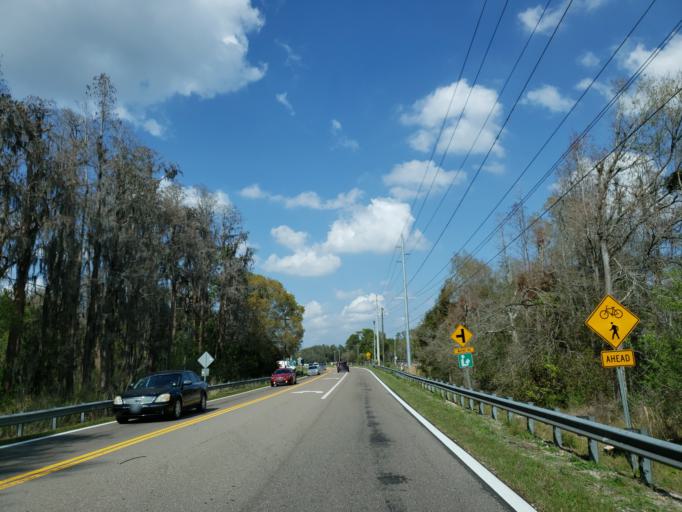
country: US
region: Florida
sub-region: Hillsborough County
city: Keystone
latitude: 28.1349
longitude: -82.5751
